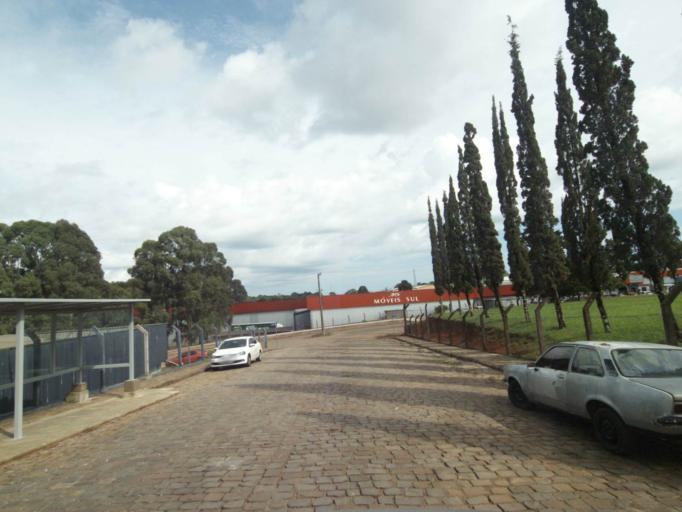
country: BR
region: Rio Grande do Sul
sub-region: Lagoa Vermelha
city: Lagoa Vermelha
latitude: -28.2273
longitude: -51.5110
